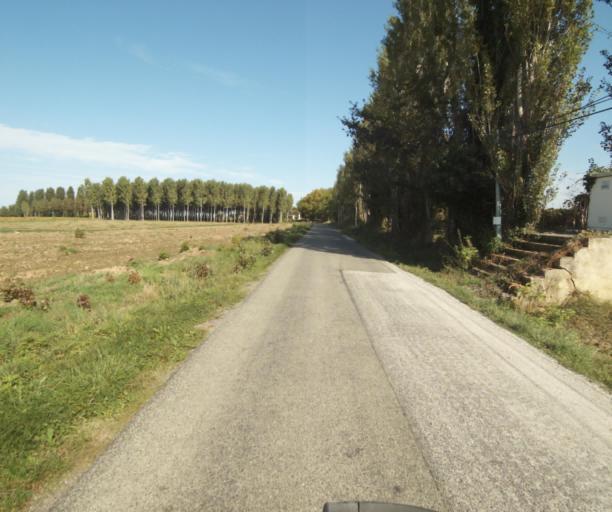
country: FR
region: Midi-Pyrenees
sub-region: Departement du Tarn-et-Garonne
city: Verdun-sur-Garonne
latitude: 43.8595
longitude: 1.2473
